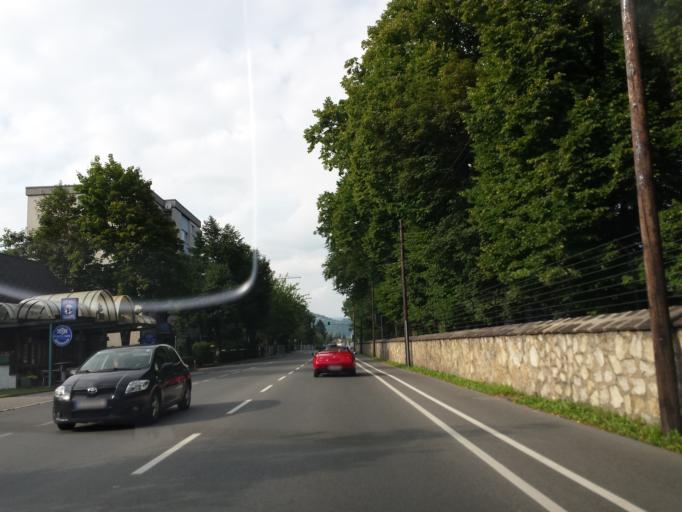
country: AT
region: Styria
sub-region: Graz Stadt
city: Wetzelsdorf
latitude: 47.0518
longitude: 15.3949
